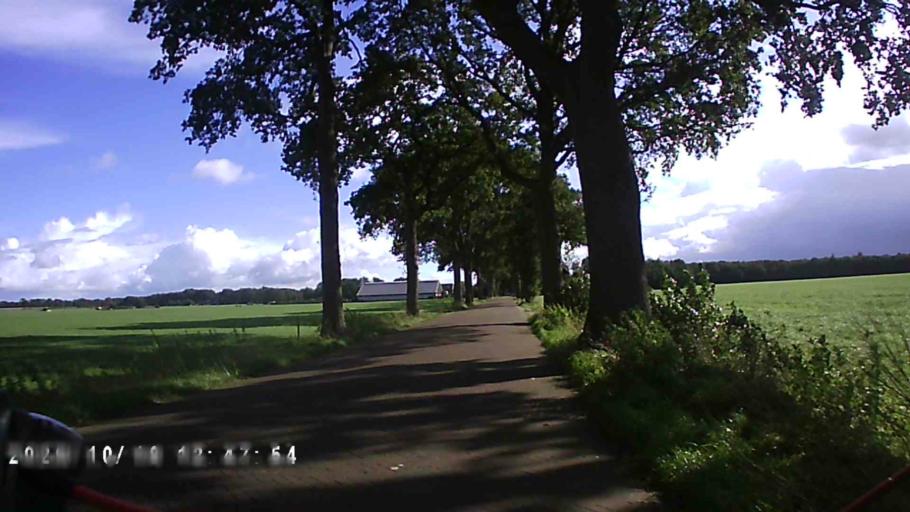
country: NL
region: Friesland
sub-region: Gemeente Weststellingwerf
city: Noordwolde
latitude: 52.9233
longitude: 6.2391
